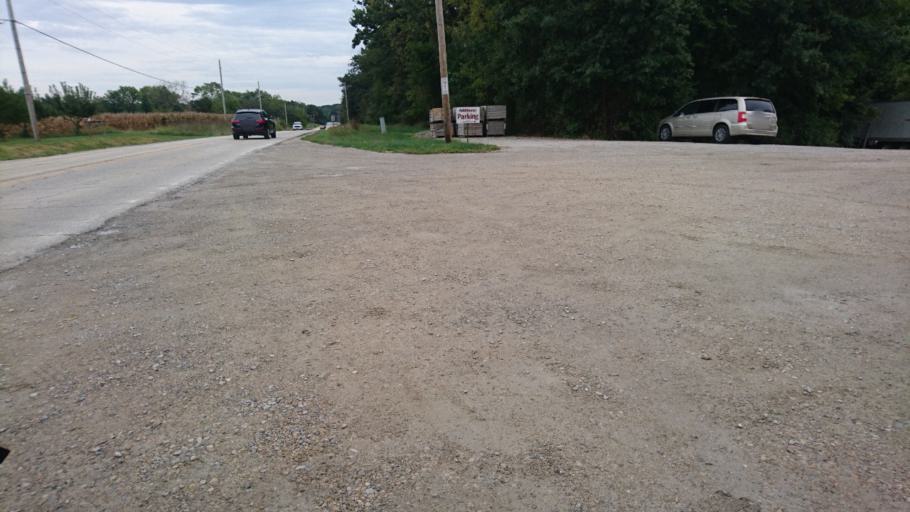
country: US
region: Illinois
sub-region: Sangamon County
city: Chatham
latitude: 39.6768
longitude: -89.6750
